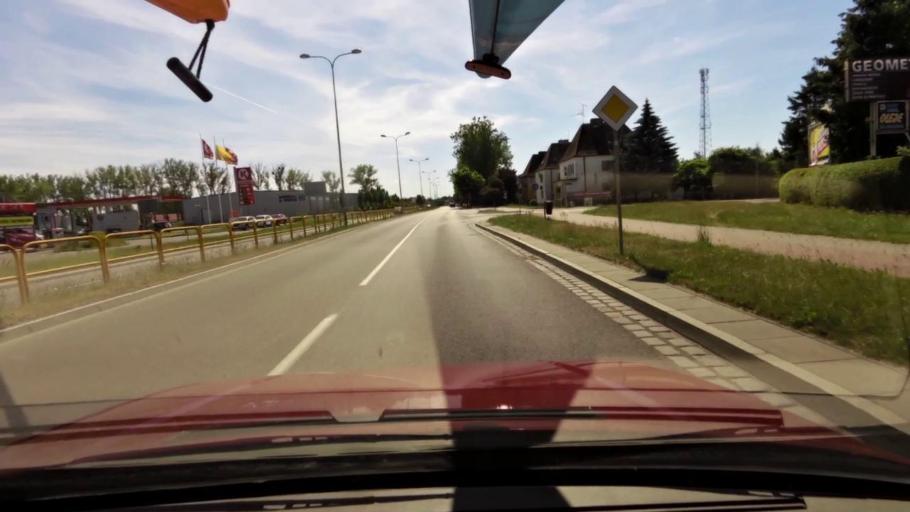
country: PL
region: Pomeranian Voivodeship
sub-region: Slupsk
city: Slupsk
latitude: 54.4518
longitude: 17.0161
